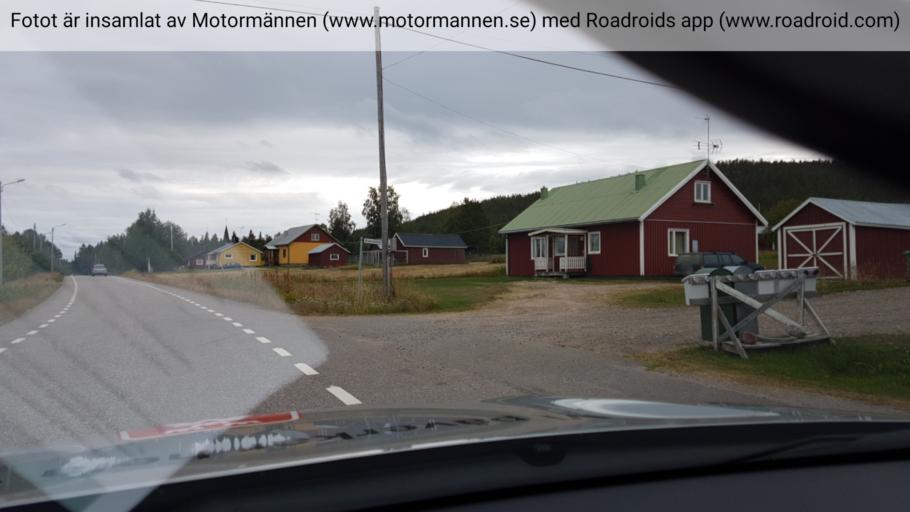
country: SE
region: Norrbotten
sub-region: Gallivare Kommun
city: Gaellivare
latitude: 67.0190
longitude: 21.8113
